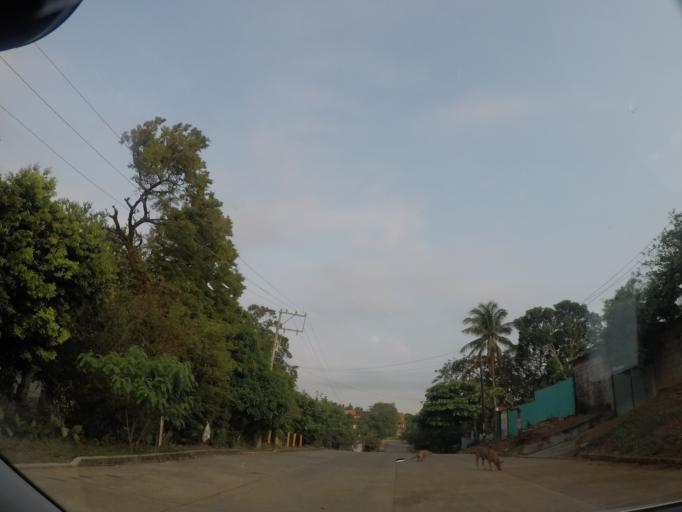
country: MX
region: Oaxaca
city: Matias Romero
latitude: 16.8720
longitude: -95.0435
